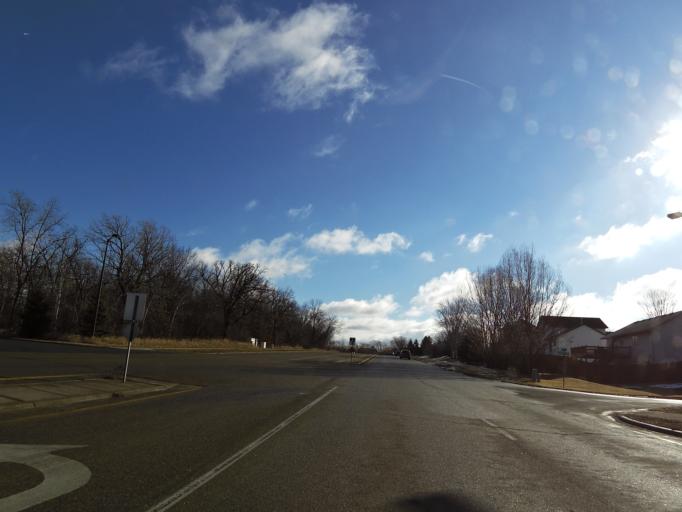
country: US
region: Minnesota
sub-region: Scott County
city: Savage
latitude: 44.7609
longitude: -93.3755
